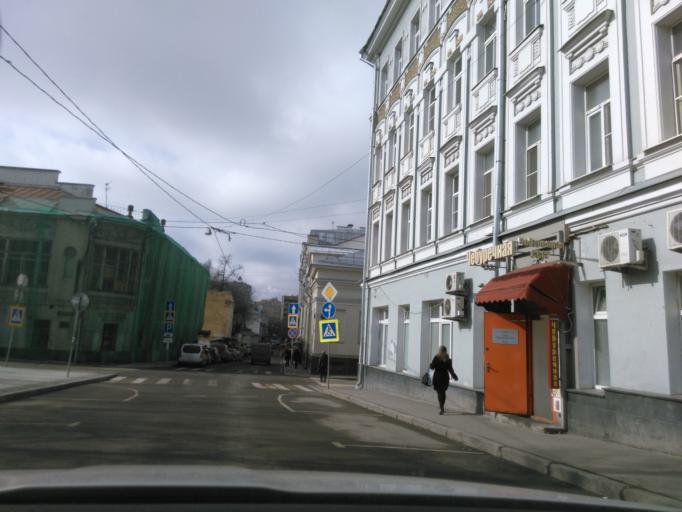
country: RU
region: Moscow
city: Moscow
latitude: 55.7641
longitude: 37.6028
